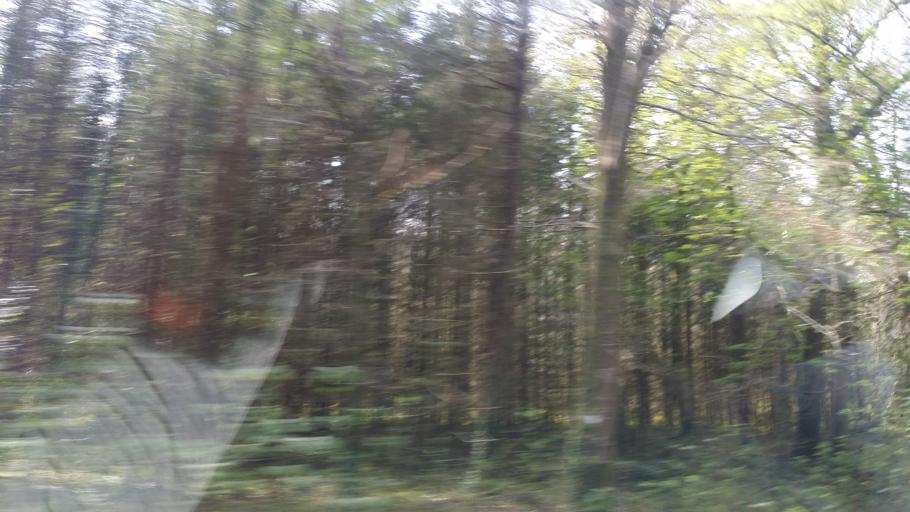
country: GB
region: Northern Ireland
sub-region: Fermanagh District
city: Enniskillen
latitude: 54.3953
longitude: -7.7070
